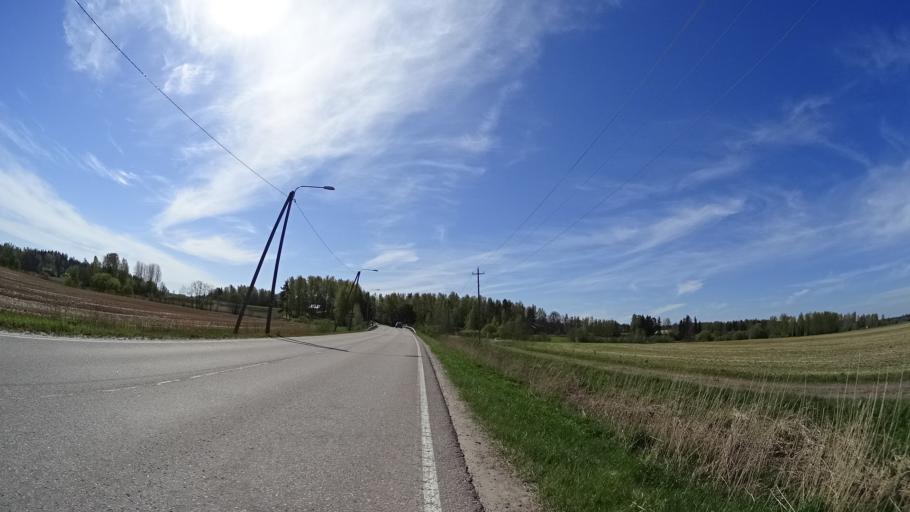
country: FI
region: Uusimaa
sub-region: Helsinki
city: Nurmijaervi
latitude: 60.3601
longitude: 24.8581
